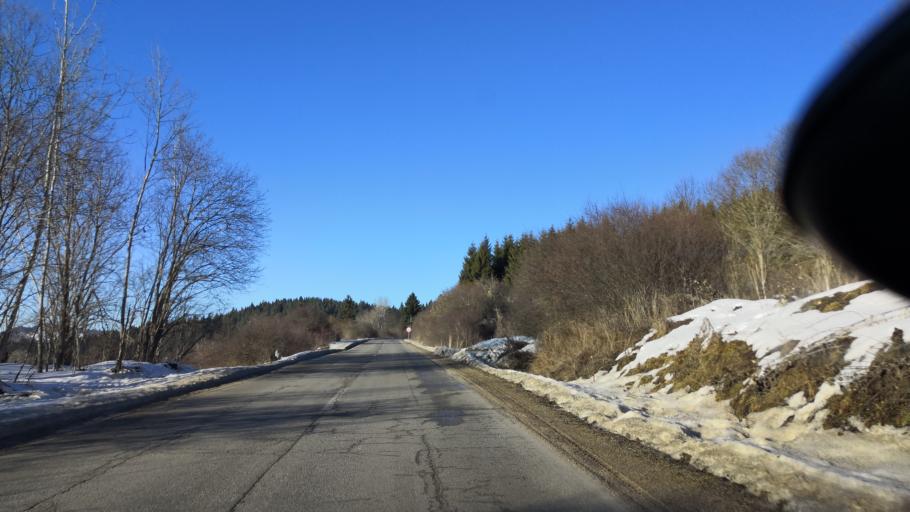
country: BA
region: Republika Srpska
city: Han Pijesak
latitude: 44.0171
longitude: 18.8839
